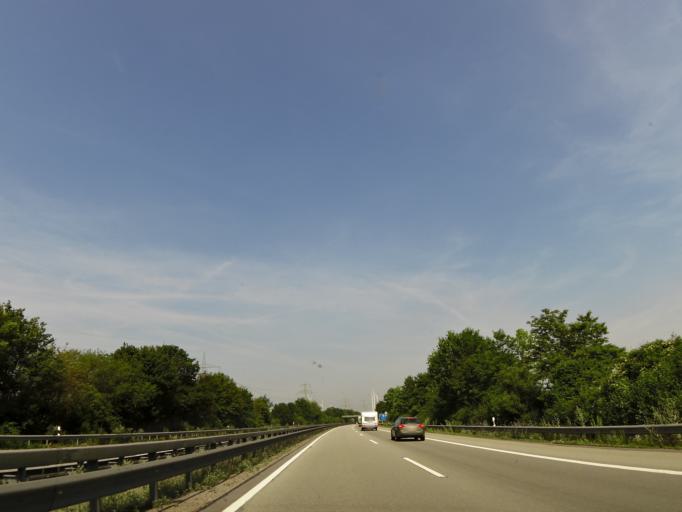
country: DE
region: Rheinland-Pfalz
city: Bornheim
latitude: 49.7961
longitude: 8.0686
